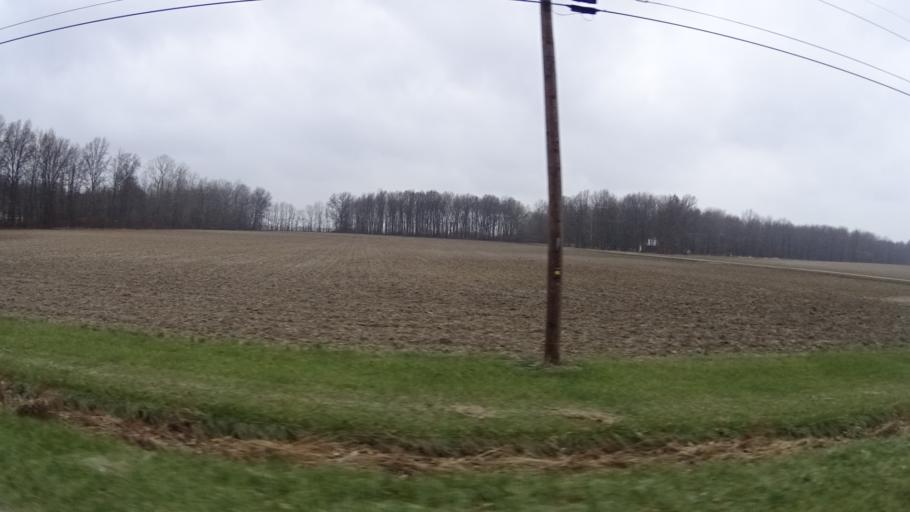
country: US
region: Ohio
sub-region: Lorain County
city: South Amherst
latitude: 41.3244
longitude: -82.2724
